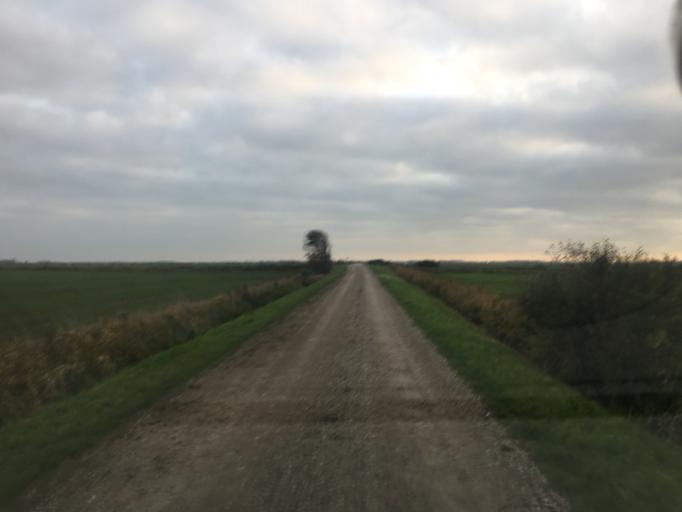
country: DE
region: Schleswig-Holstein
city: Aventoft
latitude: 54.9332
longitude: 8.7759
